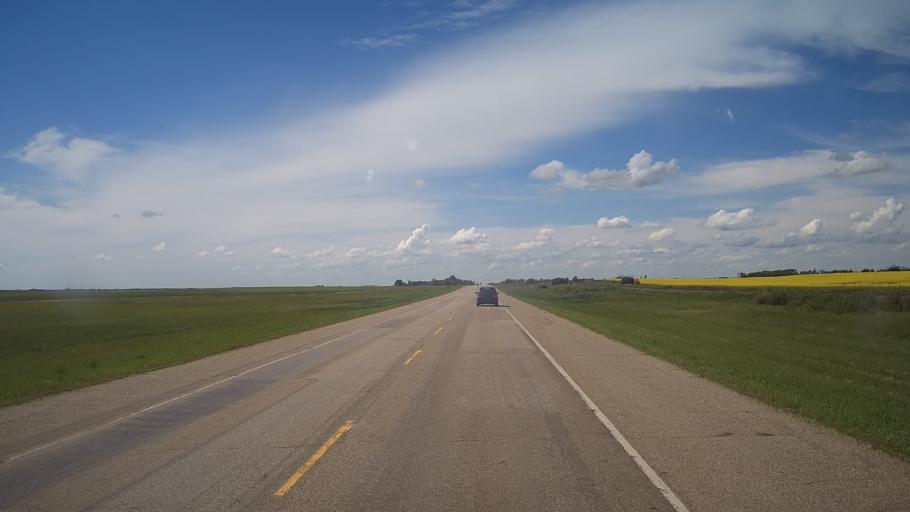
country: CA
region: Saskatchewan
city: Yorkton
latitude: 51.0793
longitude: -102.2430
